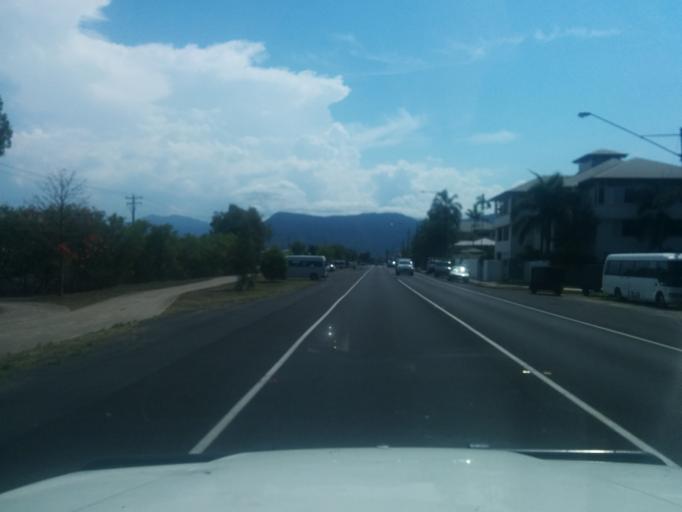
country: AU
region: Queensland
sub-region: Cairns
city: Cairns
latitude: -16.9321
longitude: 145.7666
